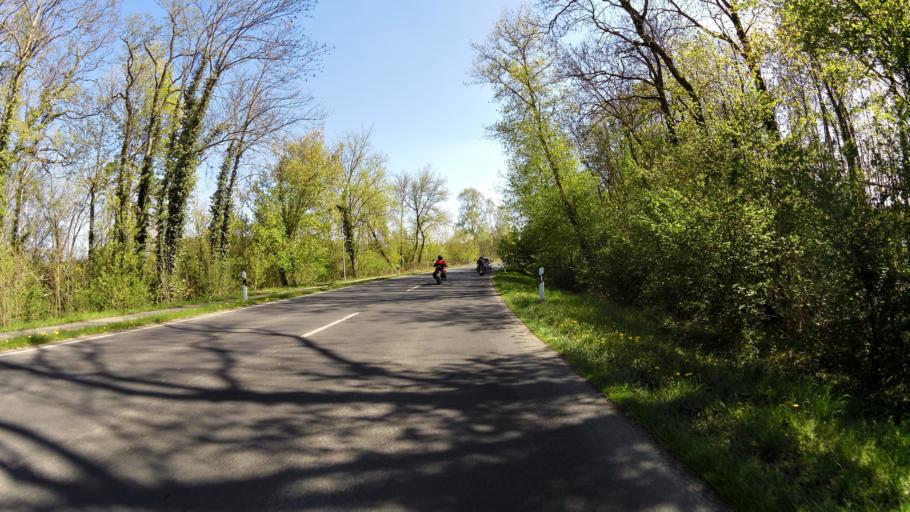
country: DE
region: Brandenburg
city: Muncheberg
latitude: 52.5212
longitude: 14.1067
